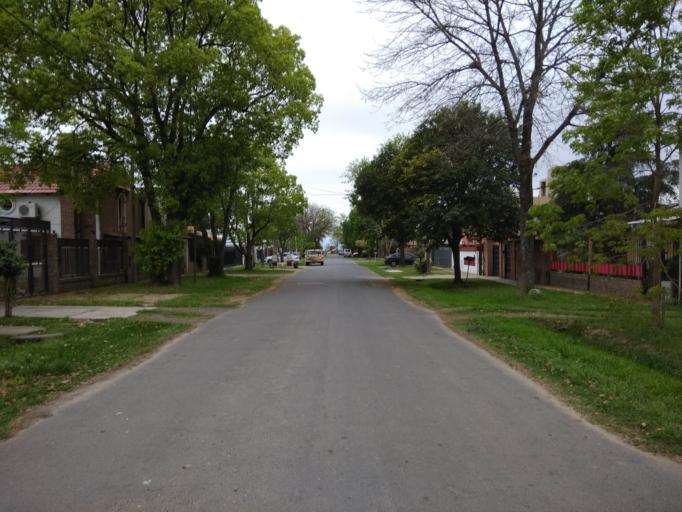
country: AR
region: Santa Fe
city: Granadero Baigorria
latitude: -32.8487
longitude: -60.6992
